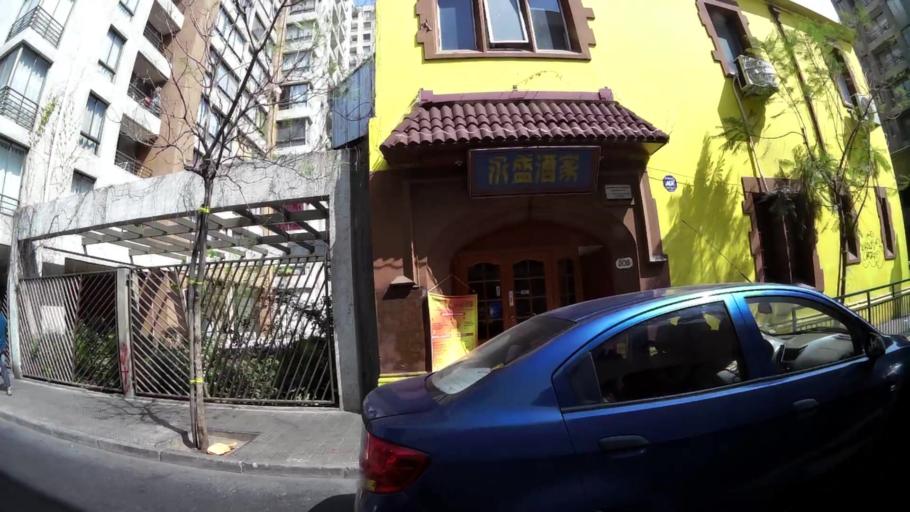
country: CL
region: Santiago Metropolitan
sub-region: Provincia de Santiago
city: Santiago
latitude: -33.4492
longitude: -70.6550
